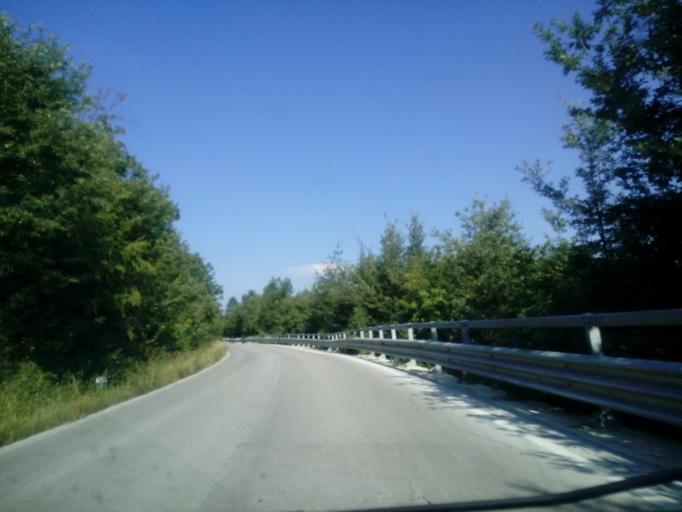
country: IT
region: Molise
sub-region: Provincia di Campobasso
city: Gildone
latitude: 41.5149
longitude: 14.7489
